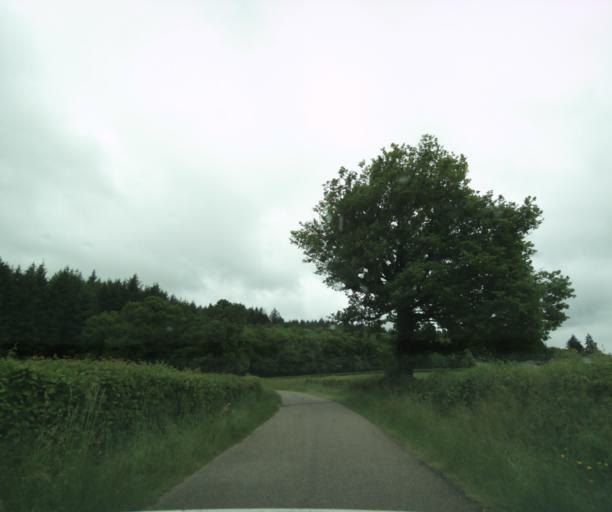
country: FR
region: Bourgogne
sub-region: Departement de Saone-et-Loire
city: Matour
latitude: 46.4318
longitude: 4.4442
